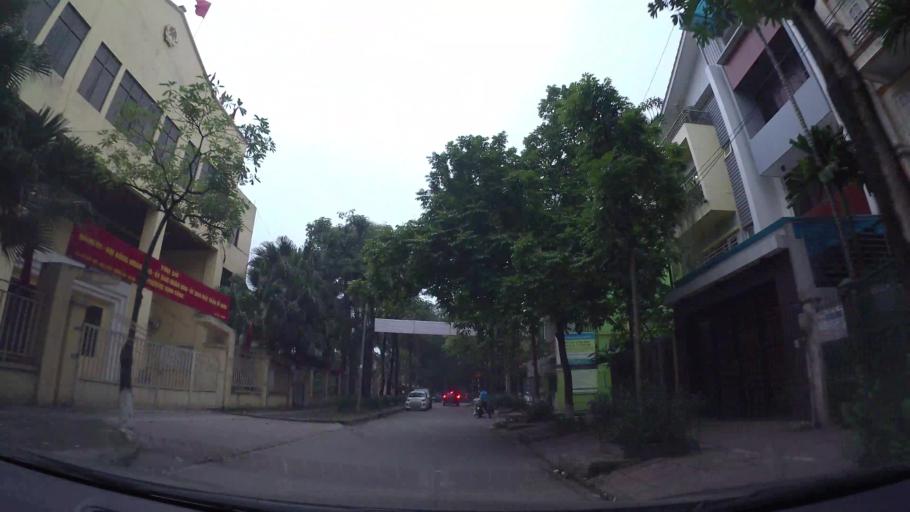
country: VN
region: Ha Noi
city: Hai BaTrung
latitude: 20.9884
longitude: 105.8320
